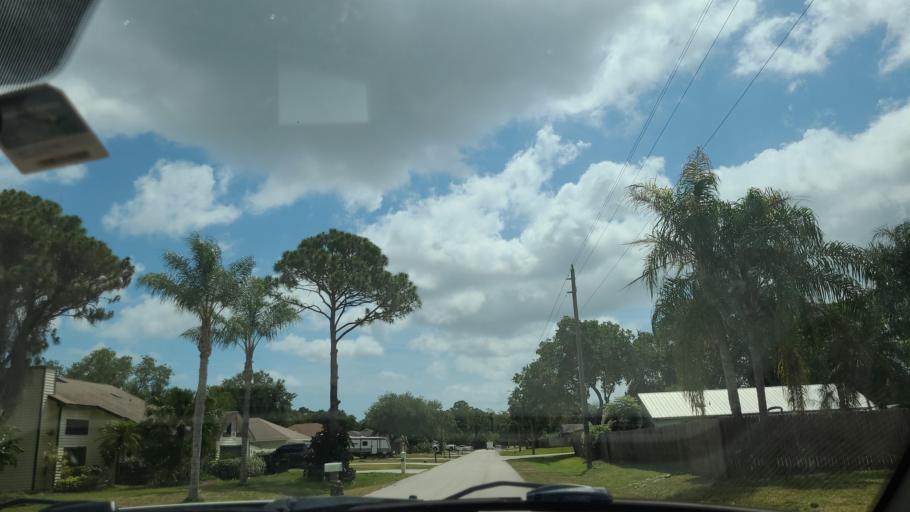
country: US
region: Florida
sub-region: Brevard County
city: West Melbourne
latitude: 28.0031
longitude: -80.6619
